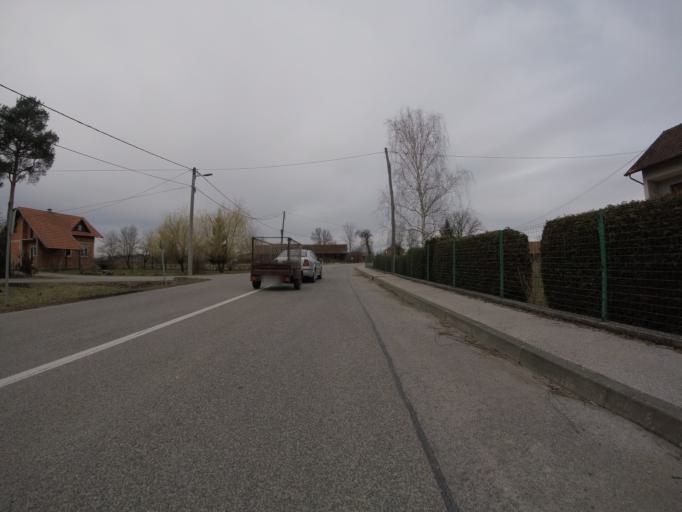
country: HR
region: Grad Zagreb
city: Horvati
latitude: 45.5747
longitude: 15.8610
